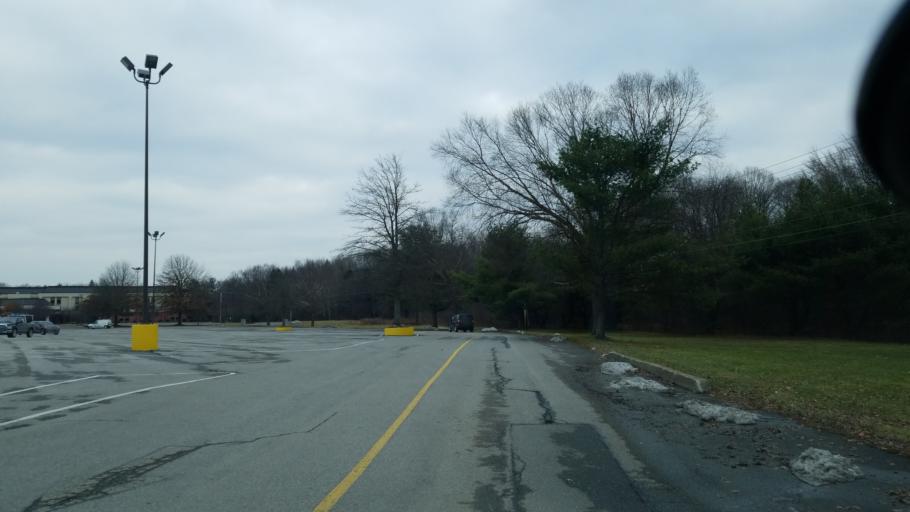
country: US
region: Pennsylvania
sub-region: Clearfield County
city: DuBois
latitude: 41.1195
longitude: -78.7241
